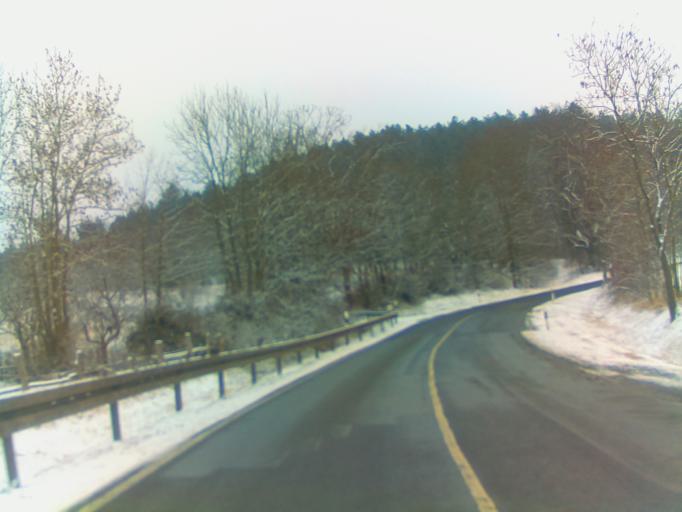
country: DE
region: Thuringia
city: Stadtilm
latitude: 50.7727
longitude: 11.0956
